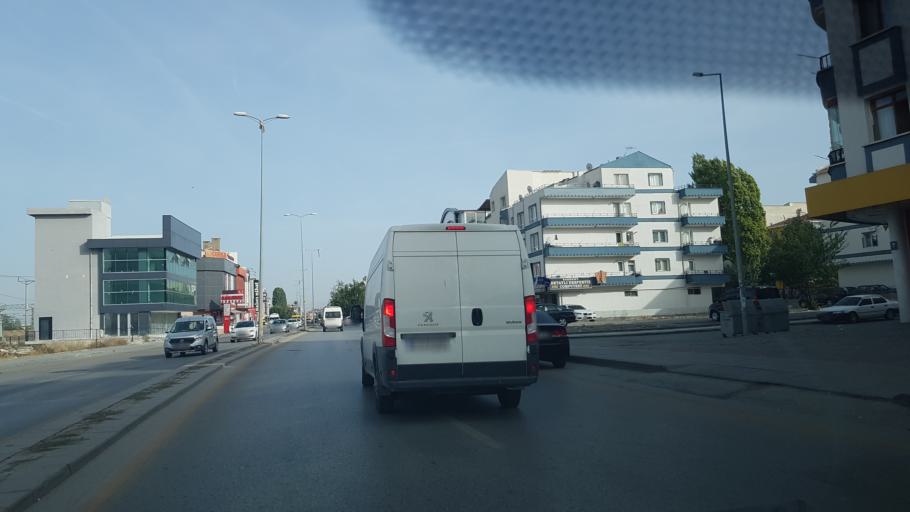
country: TR
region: Ankara
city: Etimesgut
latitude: 39.9524
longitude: 32.6438
